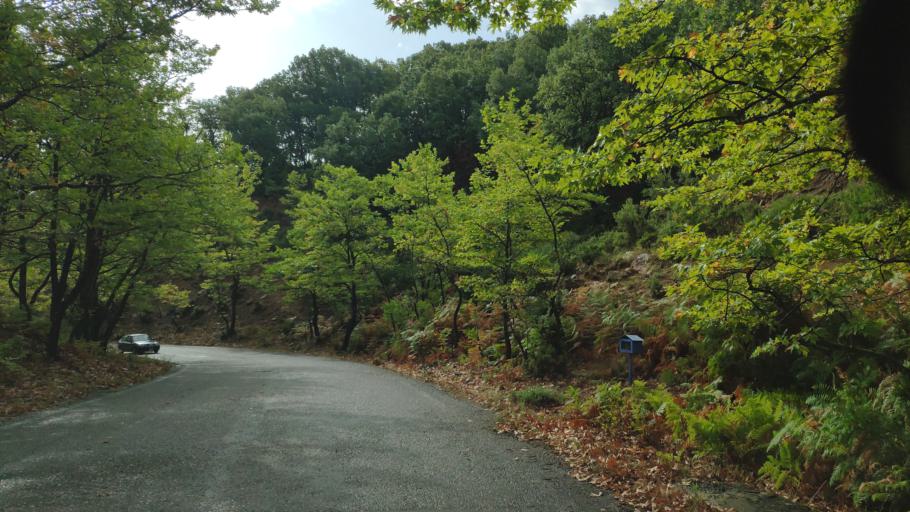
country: GR
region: West Greece
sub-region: Nomos Aitolias kai Akarnanias
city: Sardinia
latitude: 38.8647
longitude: 21.2982
